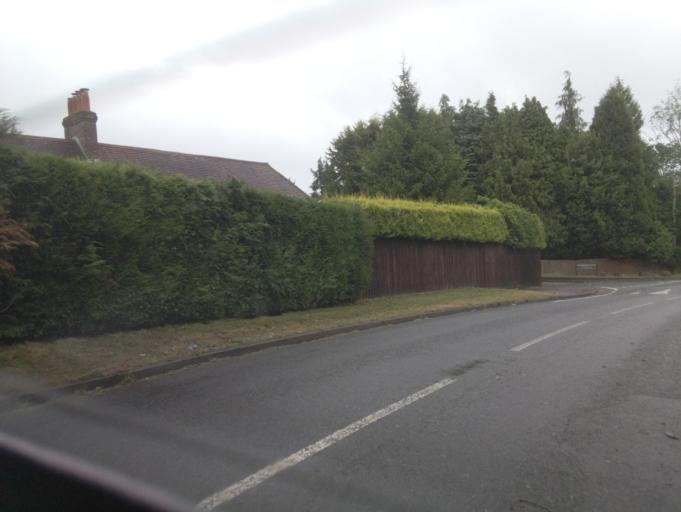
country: GB
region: England
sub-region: Surrey
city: Reigate
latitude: 51.2489
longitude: -0.1965
